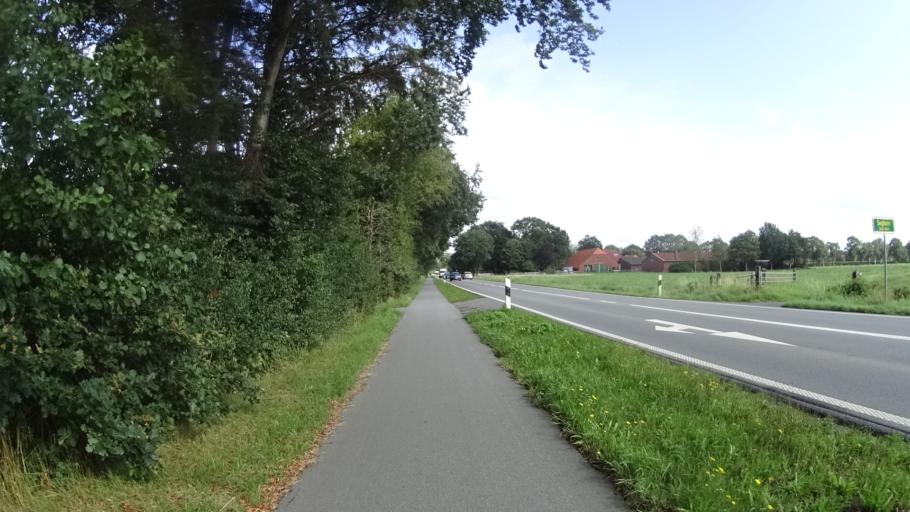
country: DE
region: Lower Saxony
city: Bockhorn
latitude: 53.3893
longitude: 8.0398
